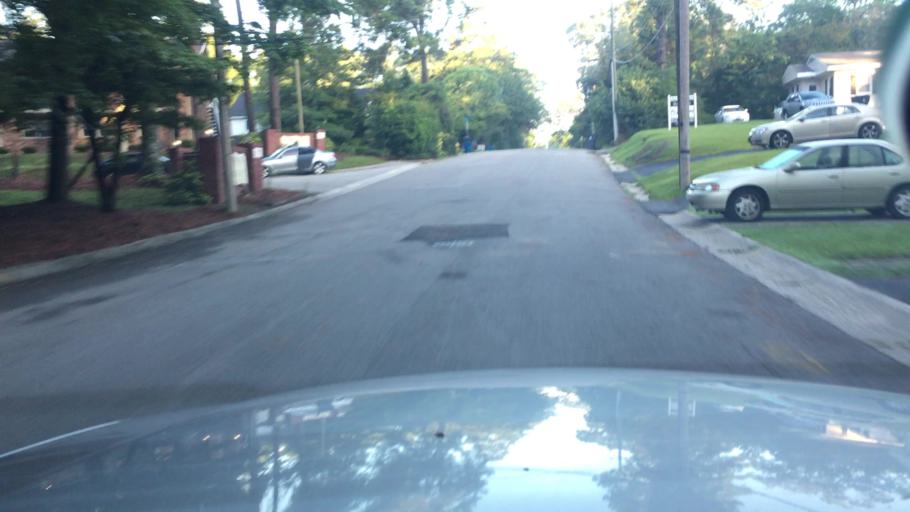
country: US
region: North Carolina
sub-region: Cumberland County
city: Fayetteville
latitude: 35.0682
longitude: -78.9142
